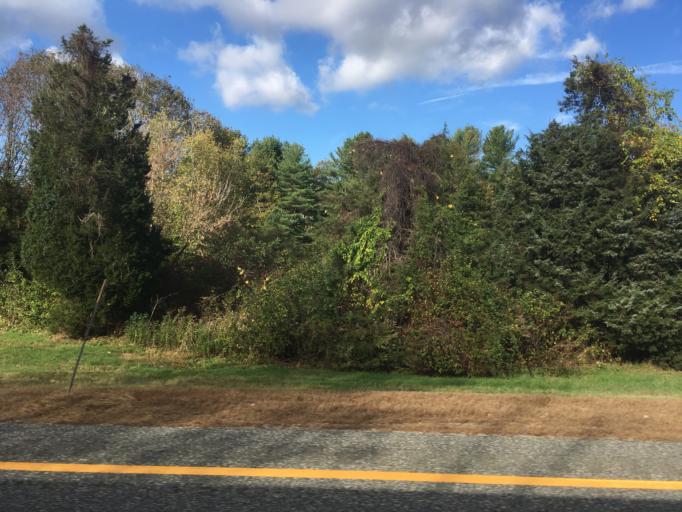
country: US
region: Rhode Island
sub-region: Kent County
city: West Warwick
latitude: 41.7432
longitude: -71.4871
